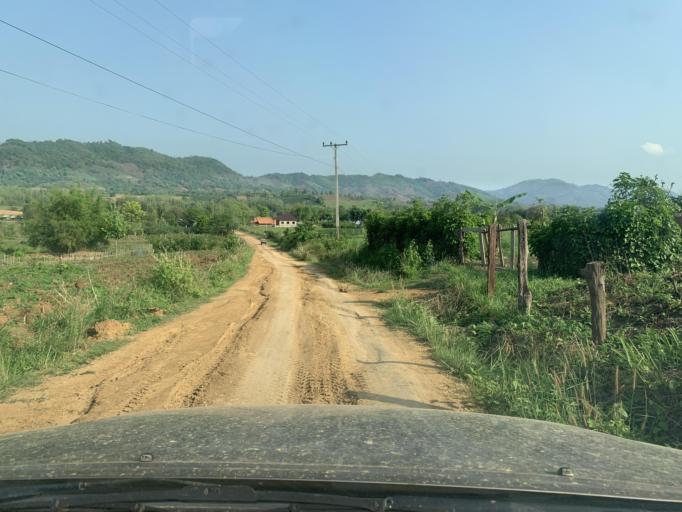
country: TH
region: Uttaradit
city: Ban Khok
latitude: 18.2727
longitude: 101.3065
